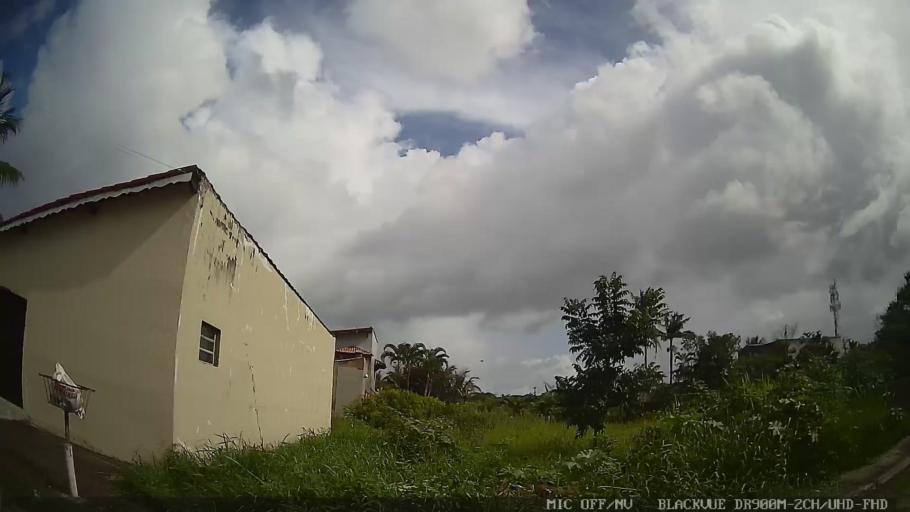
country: BR
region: Sao Paulo
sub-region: Itanhaem
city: Itanhaem
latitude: -24.2345
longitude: -46.8799
